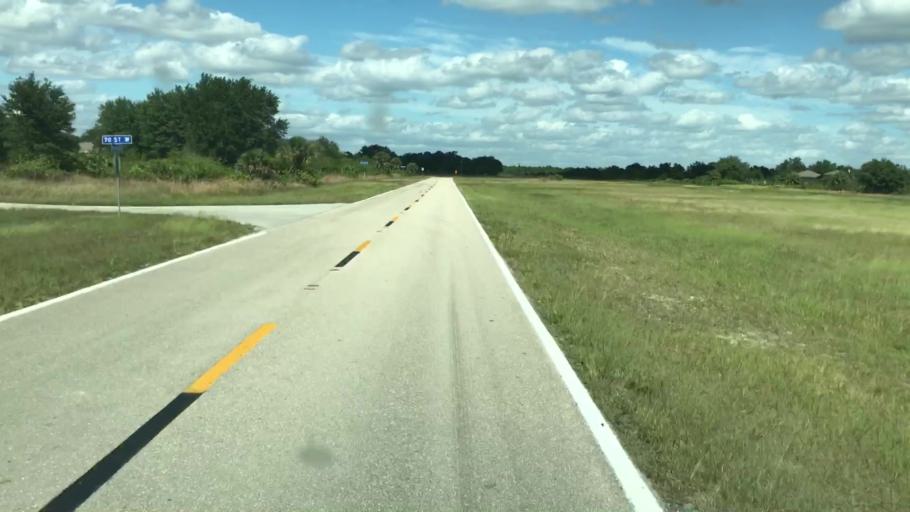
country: US
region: Florida
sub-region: Lee County
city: Olga
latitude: 26.6809
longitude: -81.6637
